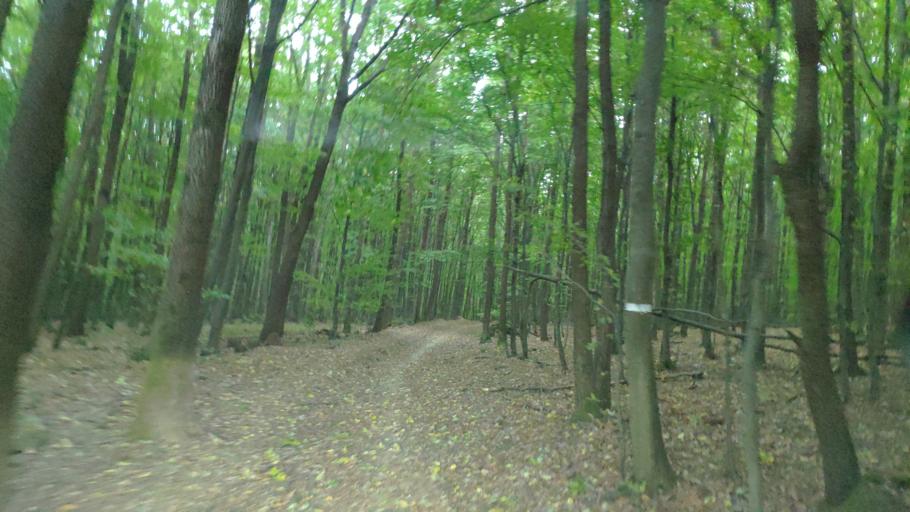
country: SK
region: Kosicky
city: Kosice
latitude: 48.6999
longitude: 21.1942
